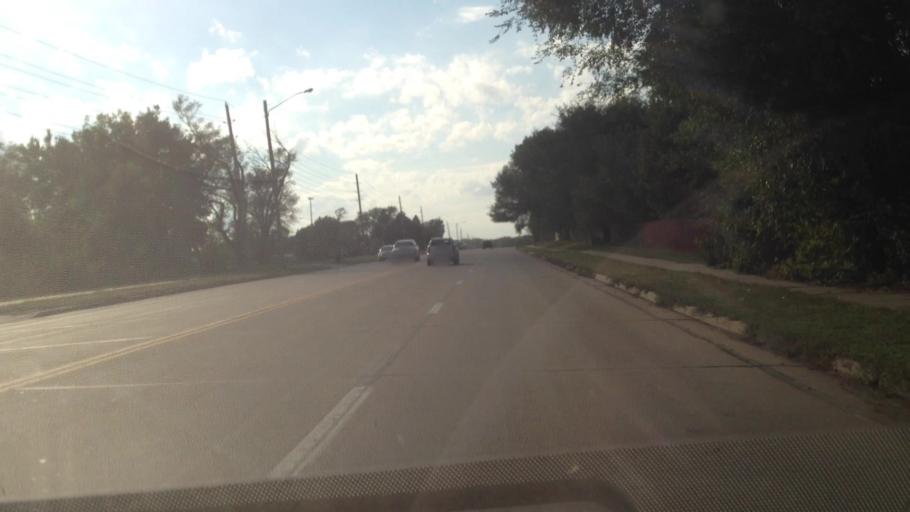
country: US
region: Kansas
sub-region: Douglas County
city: Lawrence
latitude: 38.9282
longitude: -95.2706
